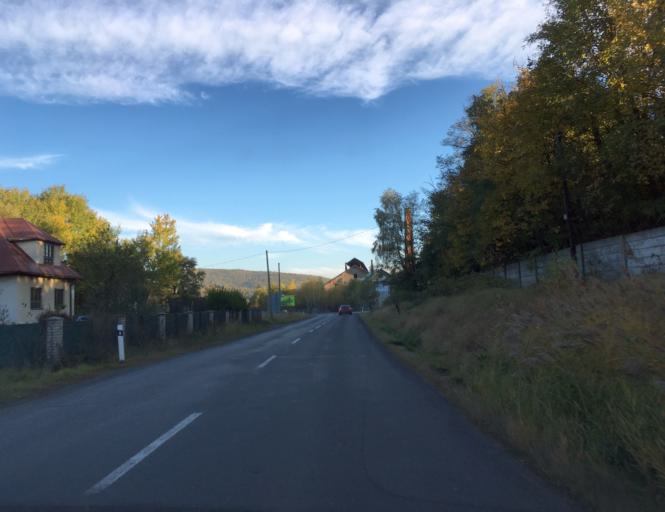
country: SK
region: Banskobystricky
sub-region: Okres Banska Bystrica
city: Banska Stiavnica
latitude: 48.4386
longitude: 18.9205
